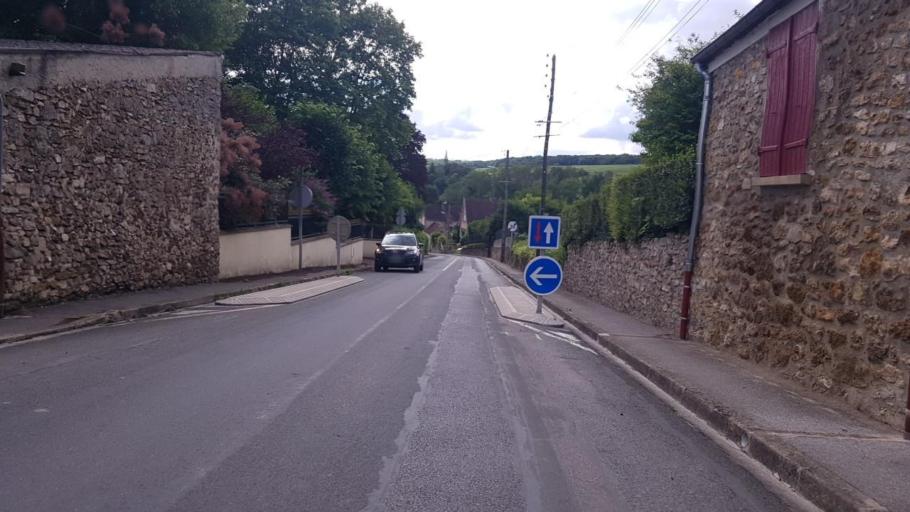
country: FR
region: Picardie
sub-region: Departement de l'Aisne
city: Crezancy
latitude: 49.0760
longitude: 3.5010
